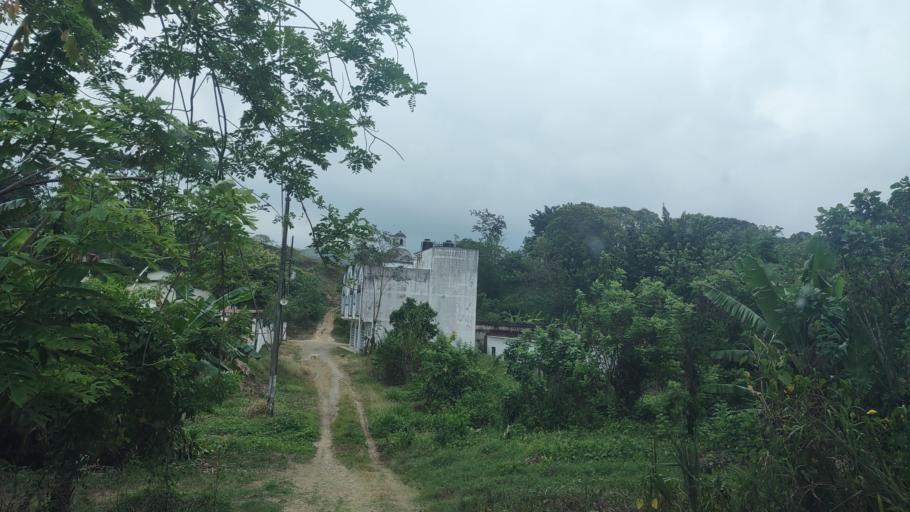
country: MX
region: Veracruz
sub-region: Uxpanapa
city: Poblado 10
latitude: 17.4517
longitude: -94.0990
